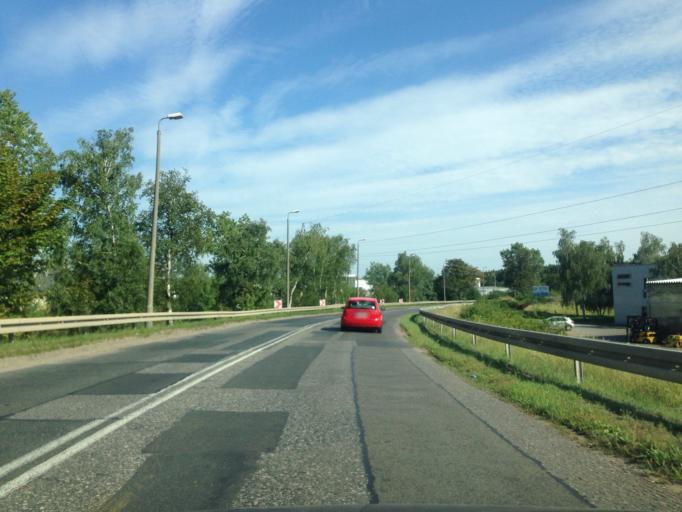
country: PL
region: Kujawsko-Pomorskie
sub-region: Torun
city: Torun
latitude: 52.9915
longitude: 18.6605
